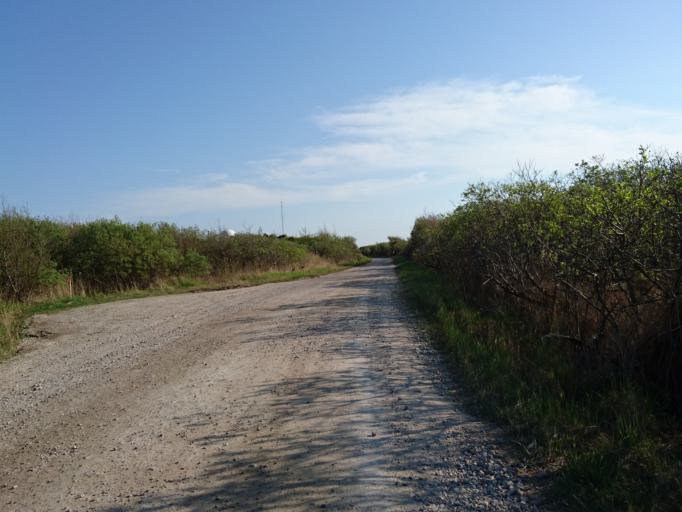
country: DK
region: North Denmark
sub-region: Frederikshavn Kommune
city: Skagen
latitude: 57.7484
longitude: 10.6033
